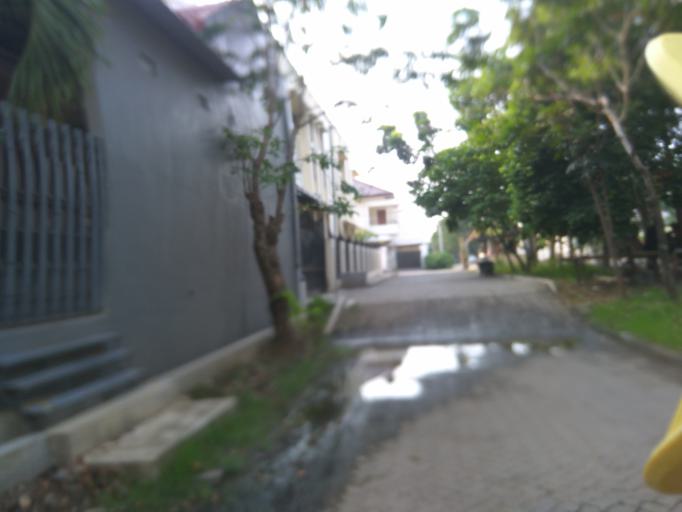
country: ID
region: Central Java
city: Semarang
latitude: -6.9697
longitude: 110.3978
